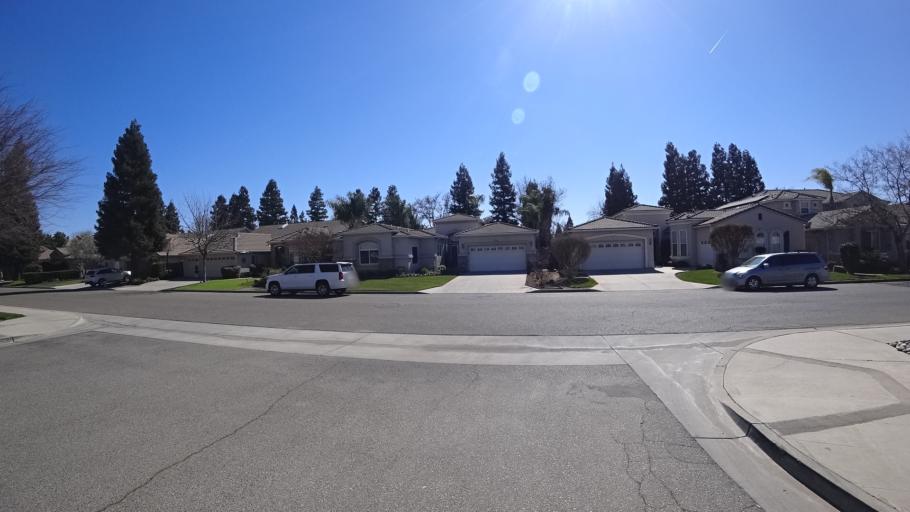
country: US
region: California
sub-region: Fresno County
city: Clovis
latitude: 36.8772
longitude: -119.7361
